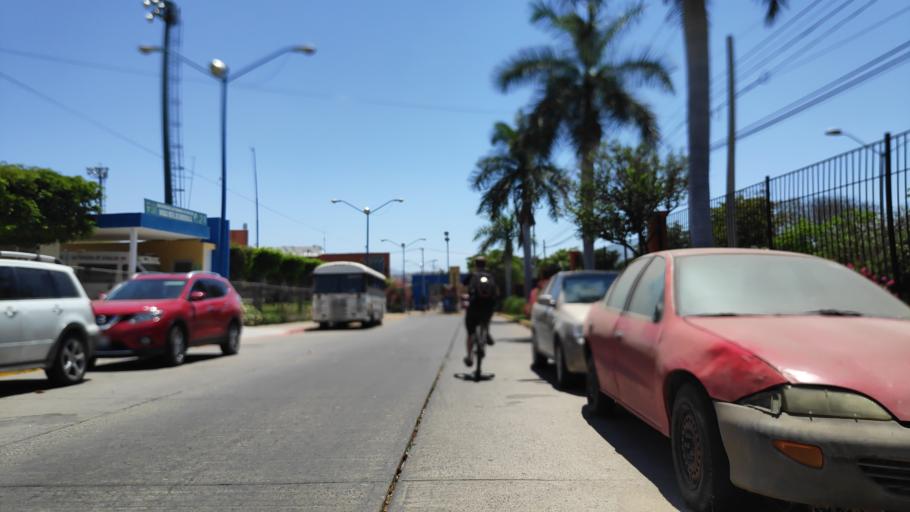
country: MX
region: Sinaloa
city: Culiacan
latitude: 24.8232
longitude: -107.3834
